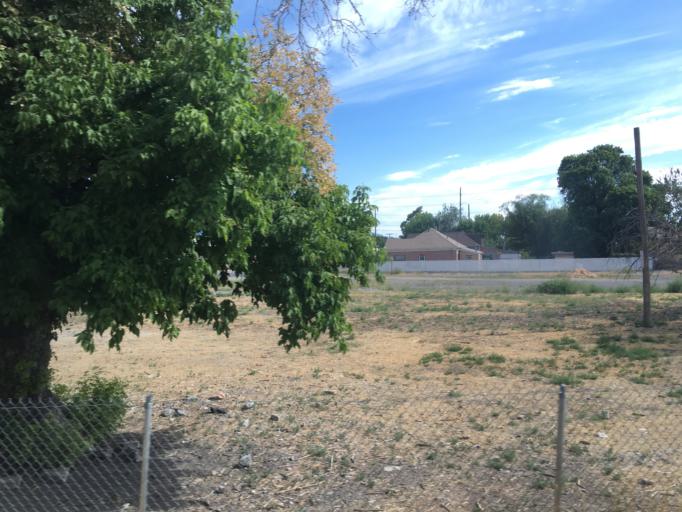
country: US
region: Utah
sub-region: Salt Lake County
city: Salt Lake City
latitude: 40.7690
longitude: -111.9088
